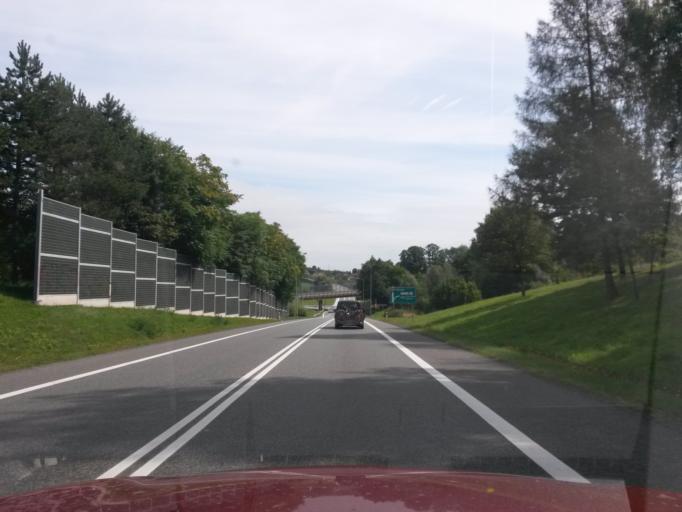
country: PL
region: Lesser Poland Voivodeship
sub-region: Powiat bochenski
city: Bochnia
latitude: 49.9578
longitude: 20.4240
